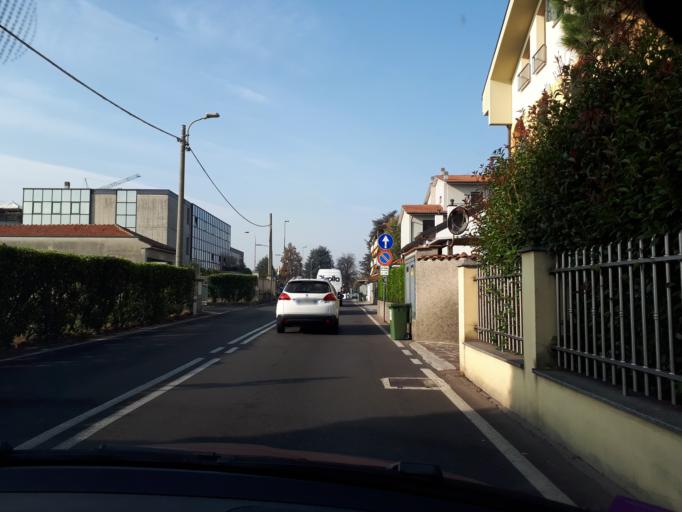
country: IT
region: Lombardy
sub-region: Provincia di Monza e Brianza
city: Biassono
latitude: 45.6274
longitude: 9.2770
